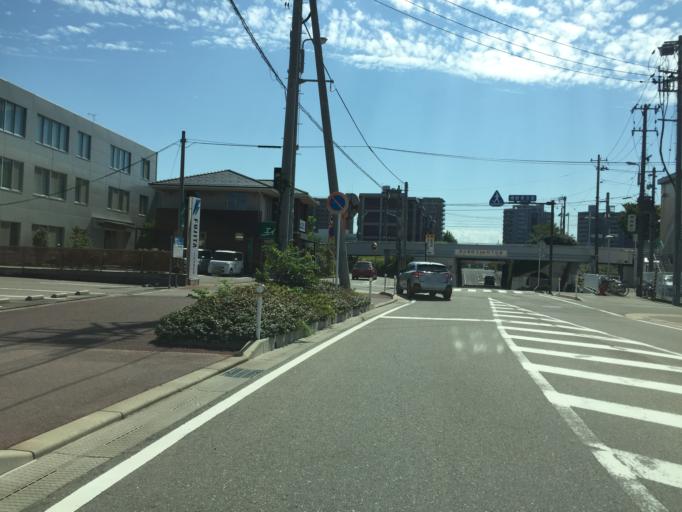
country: JP
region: Niigata
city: Niigata-shi
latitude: 37.9130
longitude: 139.0310
